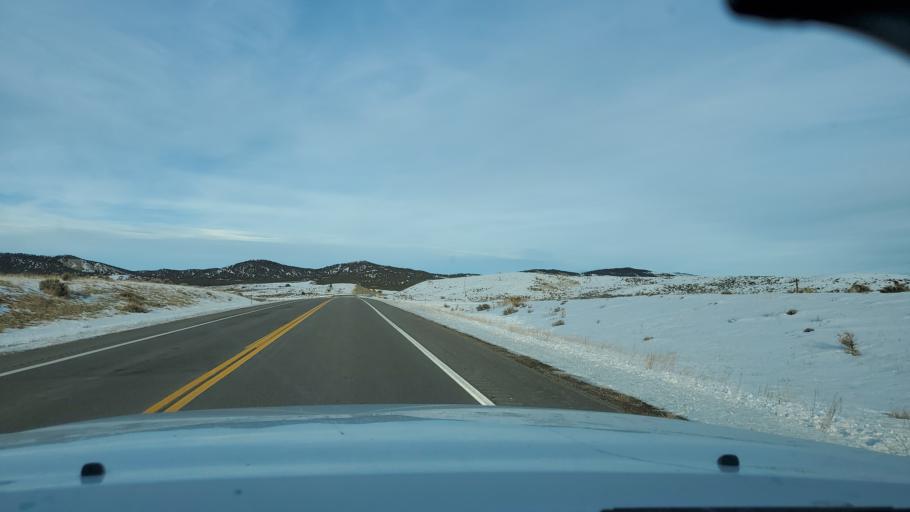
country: US
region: Colorado
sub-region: Rio Blanco County
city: Rangely
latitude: 40.3296
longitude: -108.4931
